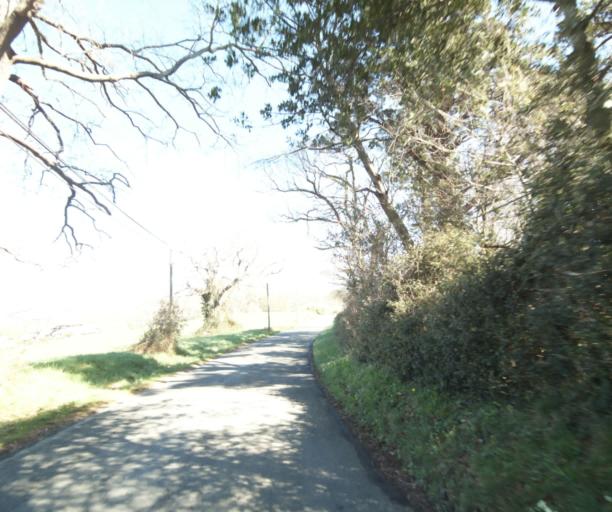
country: FR
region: Aquitaine
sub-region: Departement des Pyrenees-Atlantiques
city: Urrugne
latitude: 43.3548
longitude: -1.6990
